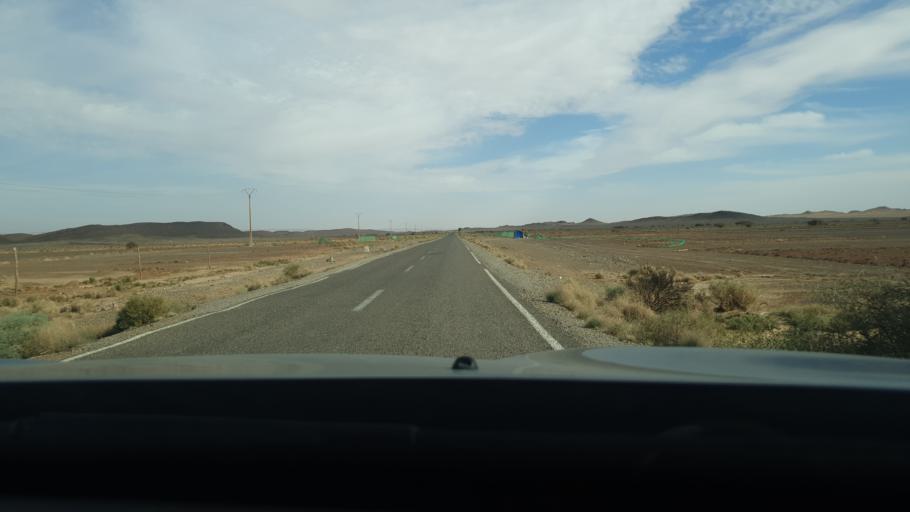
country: MA
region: Meknes-Tafilalet
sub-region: Errachidia
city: Goulmima
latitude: 31.5705
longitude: -4.8078
